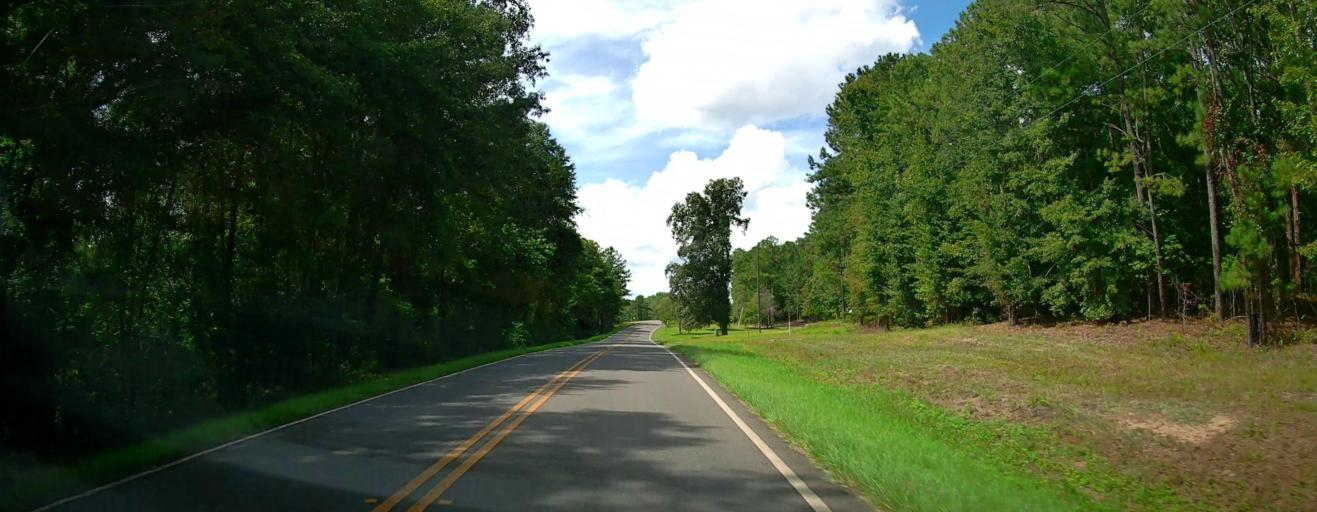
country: US
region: Georgia
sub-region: Taylor County
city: Butler
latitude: 32.5342
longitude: -84.2138
